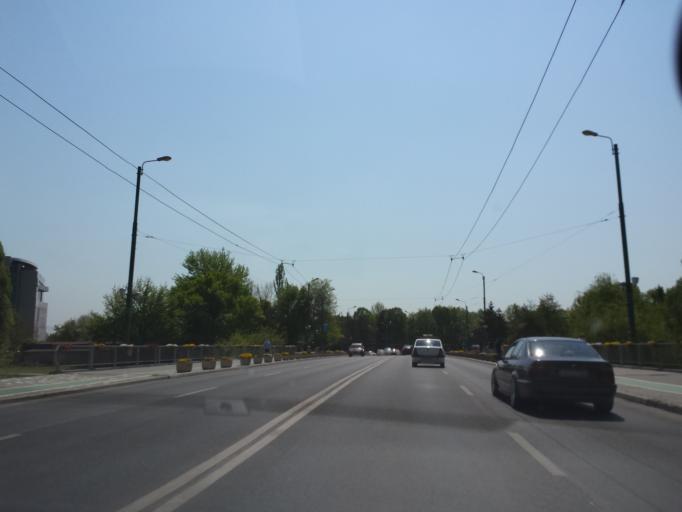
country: RO
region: Timis
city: Timisoara
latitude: 45.7507
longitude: 21.2343
